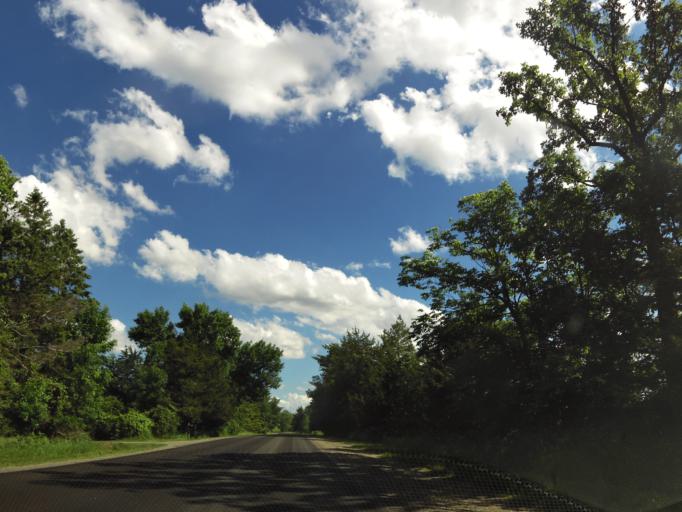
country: US
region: Minnesota
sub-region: Meeker County
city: Dassel
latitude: 45.1498
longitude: -94.3003
